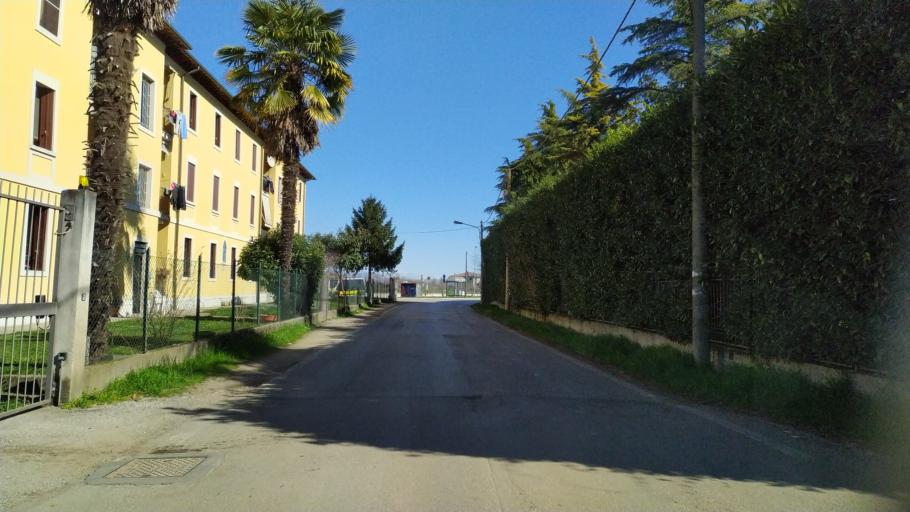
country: IT
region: Veneto
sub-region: Provincia di Vicenza
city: Monticello Conte Otto
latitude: 45.5910
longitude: 11.5430
